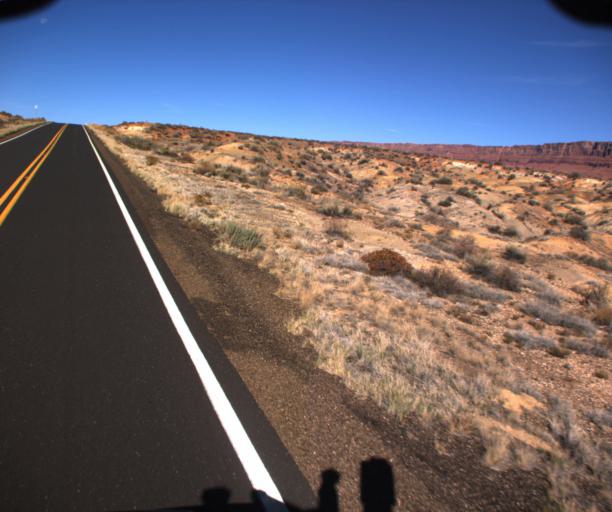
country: US
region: Arizona
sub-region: Coconino County
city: Page
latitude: 36.6901
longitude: -111.8833
